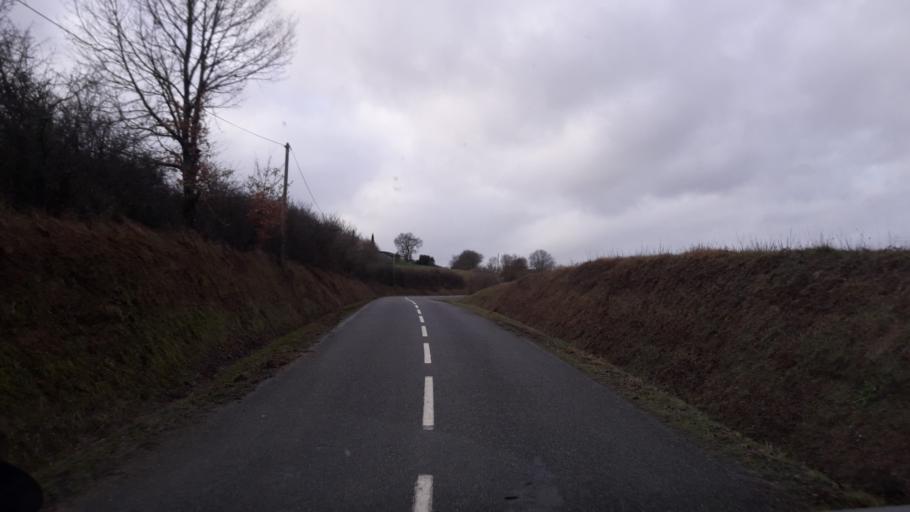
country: FR
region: Midi-Pyrenees
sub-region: Departement de la Haute-Garonne
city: Montesquieu-Volvestre
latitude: 43.2272
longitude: 1.2769
